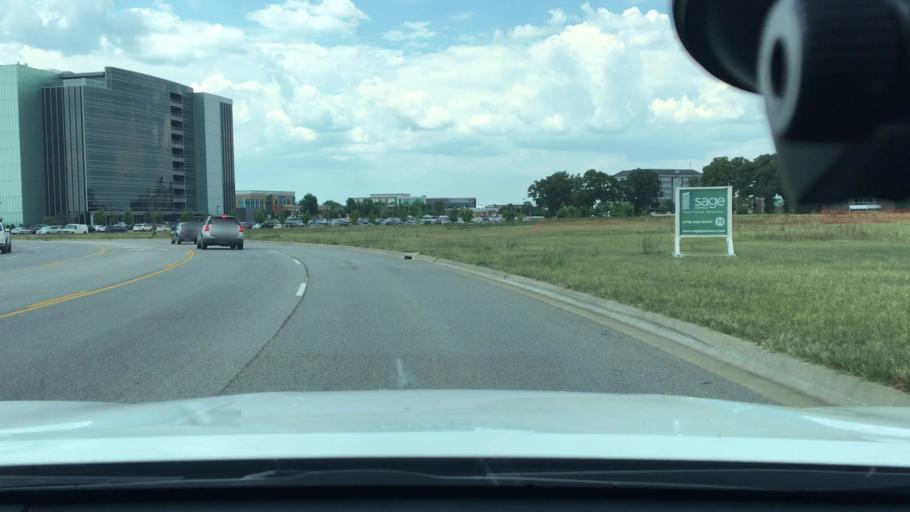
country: US
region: Arkansas
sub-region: Benton County
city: Cave Springs
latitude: 36.2995
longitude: -94.1867
